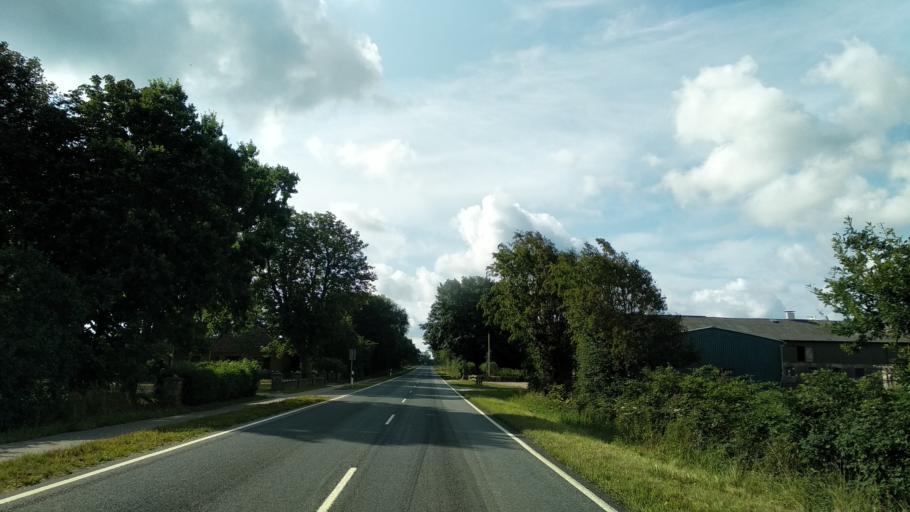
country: DE
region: Schleswig-Holstein
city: Selk
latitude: 54.4832
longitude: 9.5646
